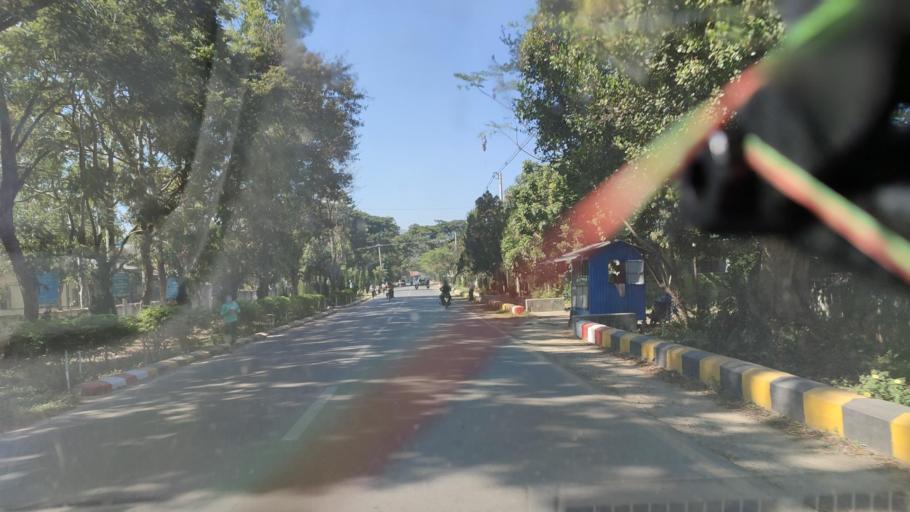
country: MM
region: Shan
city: Taunggyi
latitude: 20.6608
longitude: 96.9421
